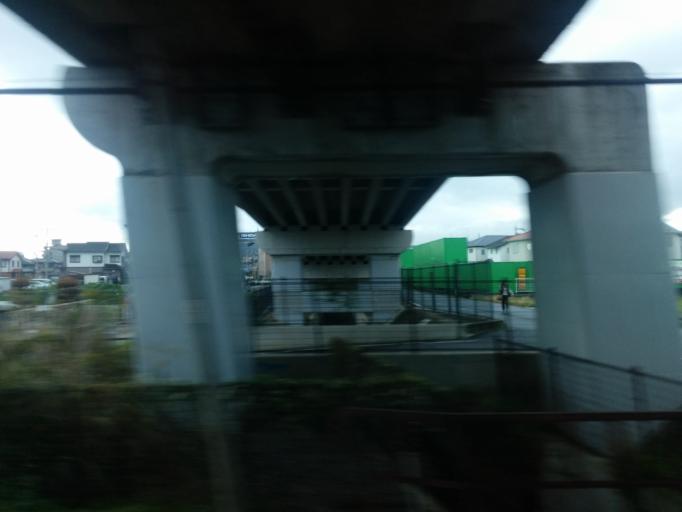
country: JP
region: Shiga Prefecture
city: Kusatsu
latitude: 35.0348
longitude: 135.9767
